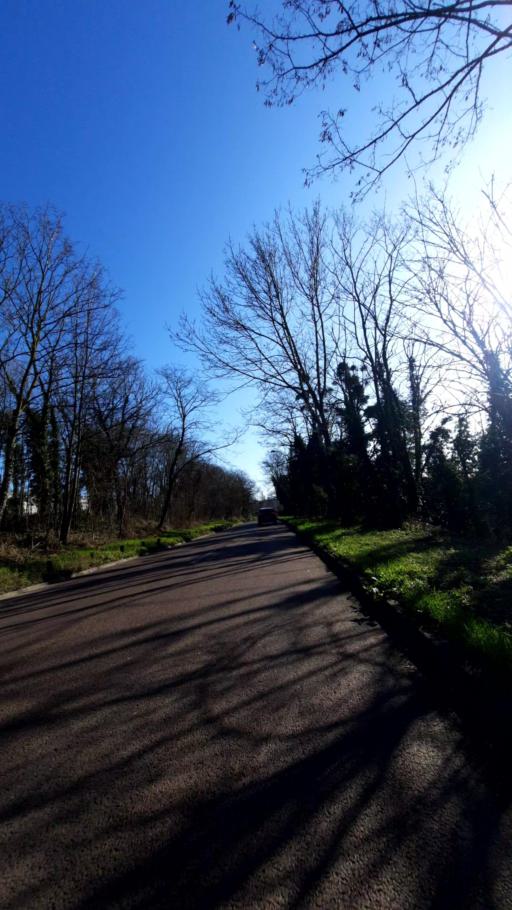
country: FR
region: Ile-de-France
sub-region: Departement du Val-de-Marne
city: Maisons-Alfort
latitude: 48.8182
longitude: 2.4523
